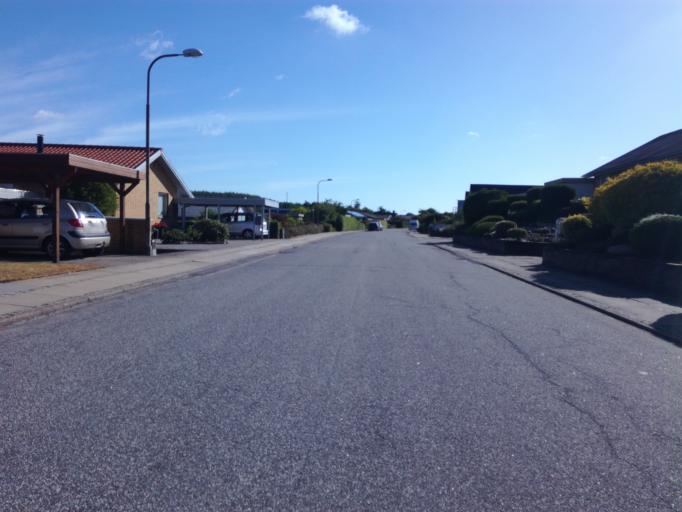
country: DK
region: South Denmark
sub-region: Fredericia Kommune
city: Fredericia
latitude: 55.5817
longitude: 9.7439
